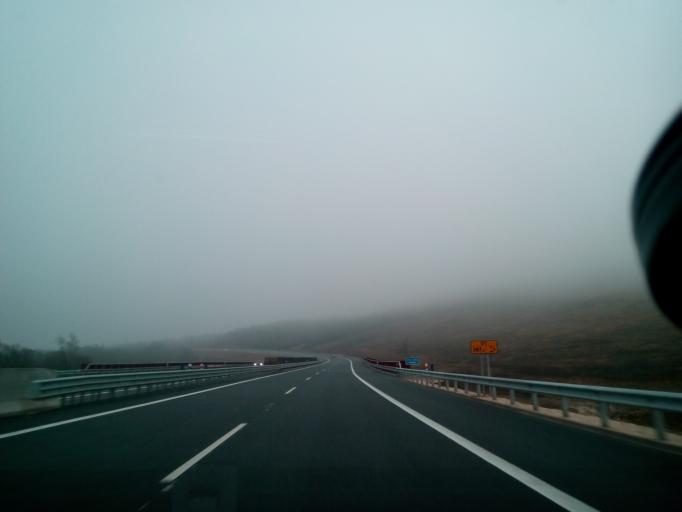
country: SK
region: Presovsky
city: Sabinov
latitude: 49.0167
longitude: 21.0391
